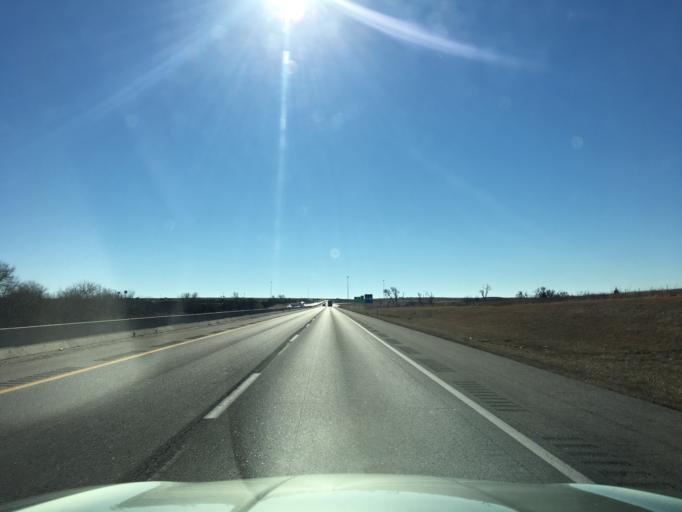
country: US
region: Kansas
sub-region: Sumner County
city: Wellington
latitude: 37.0664
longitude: -97.3385
